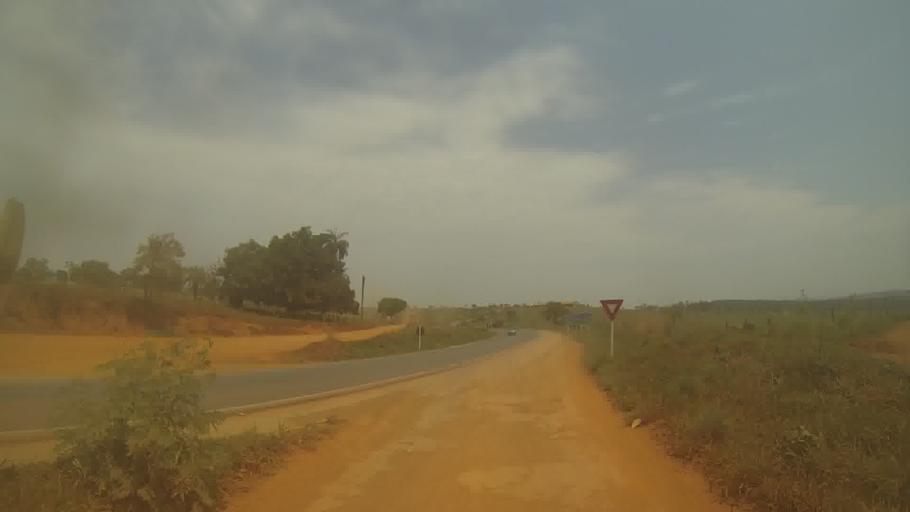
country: BR
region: Minas Gerais
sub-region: Bambui
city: Bambui
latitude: -20.0151
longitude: -45.9360
